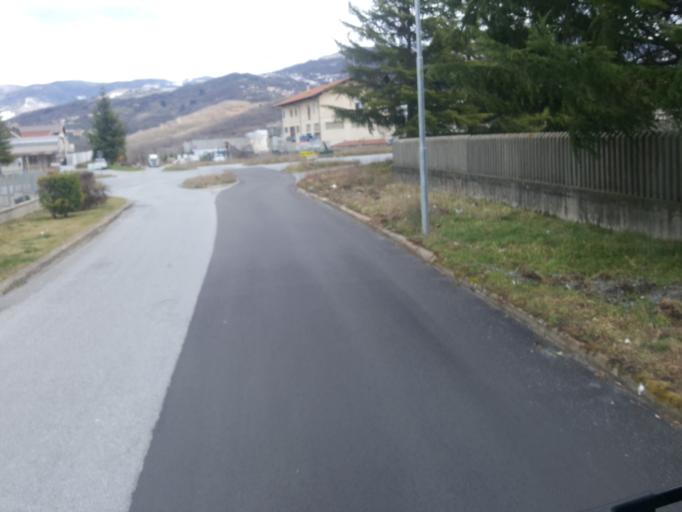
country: IT
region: Calabria
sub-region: Provincia di Cosenza
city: Figline Vegliaturo
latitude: 39.2164
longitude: 16.3091
